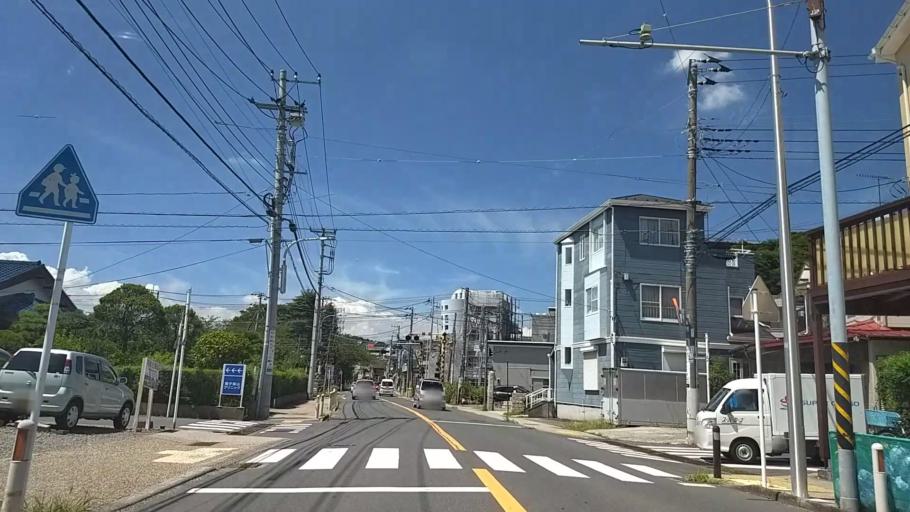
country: JP
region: Kanagawa
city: Zushi
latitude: 35.2989
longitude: 139.5946
